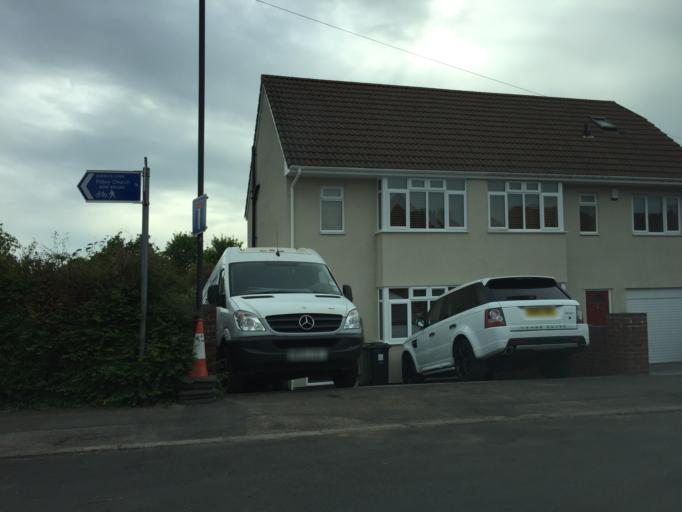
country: GB
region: England
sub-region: South Gloucestershire
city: Stoke Gifford
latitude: 51.5027
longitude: -2.5664
